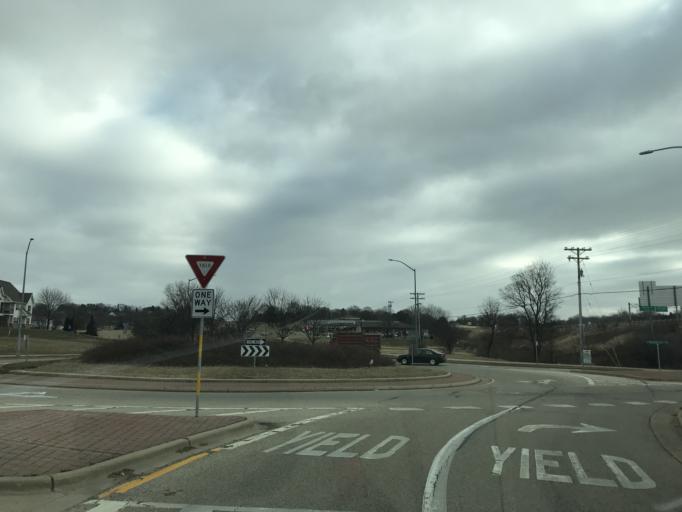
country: US
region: Wisconsin
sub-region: Dane County
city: Monona
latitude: 43.1065
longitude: -89.3011
